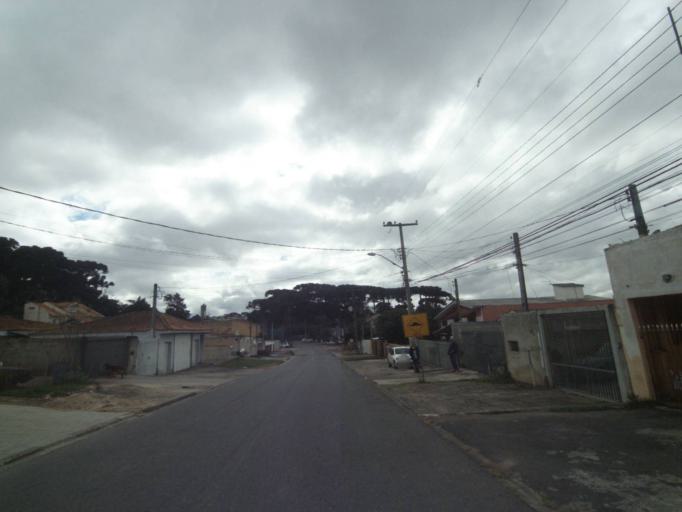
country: BR
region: Parana
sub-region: Sao Jose Dos Pinhais
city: Sao Jose dos Pinhais
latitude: -25.5373
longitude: -49.2861
